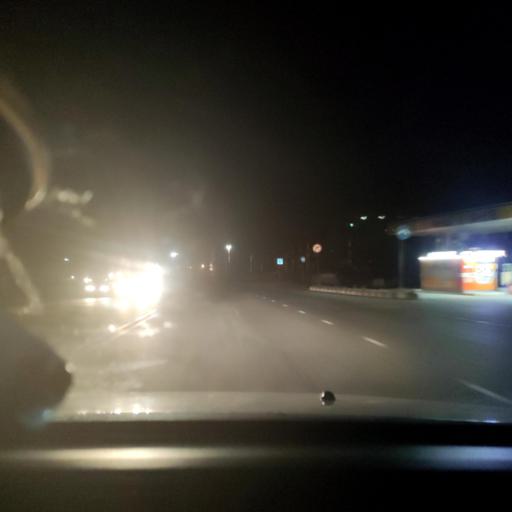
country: RU
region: Samara
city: Novokuybyshevsk
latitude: 53.0788
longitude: 49.9627
